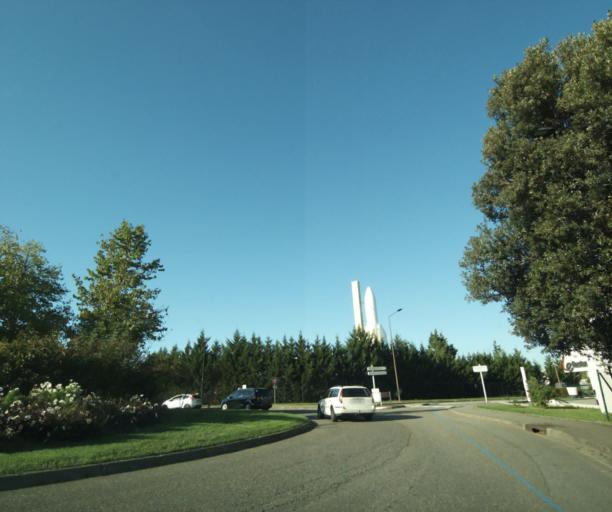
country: FR
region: Midi-Pyrenees
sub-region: Departement de la Haute-Garonne
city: Balma
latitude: 43.5840
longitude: 1.4928
